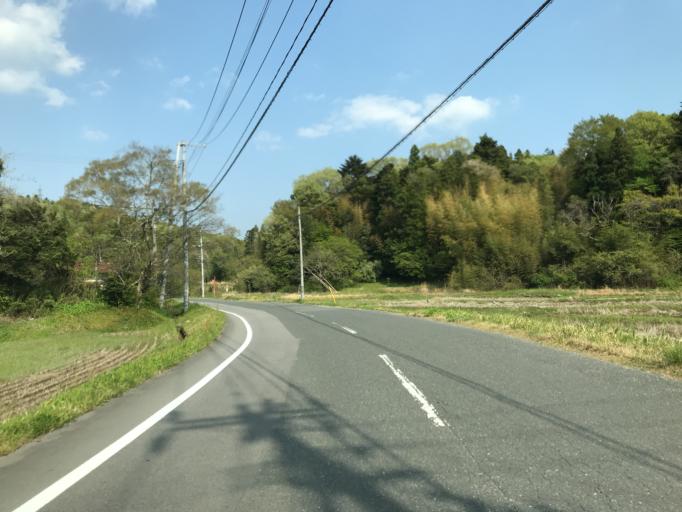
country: JP
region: Fukushima
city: Iwaki
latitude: 36.9693
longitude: 140.7609
